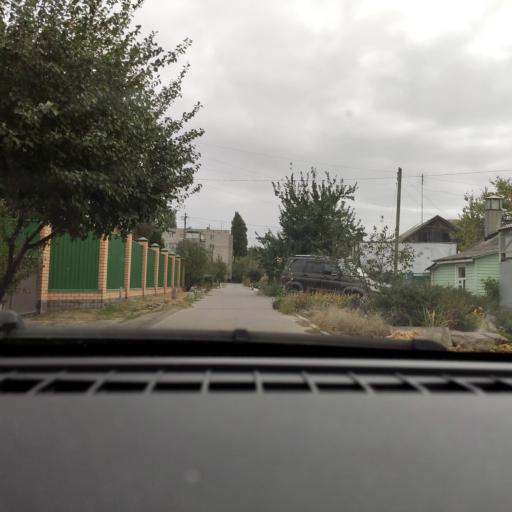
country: RU
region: Voronezj
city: Voronezh
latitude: 51.6597
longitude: 39.2747
